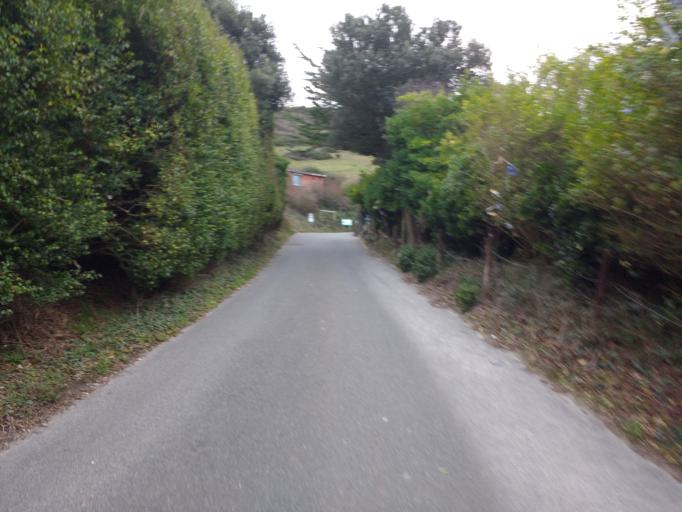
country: GB
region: England
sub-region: Isle of Wight
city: Totland
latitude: 50.6665
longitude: -1.5658
